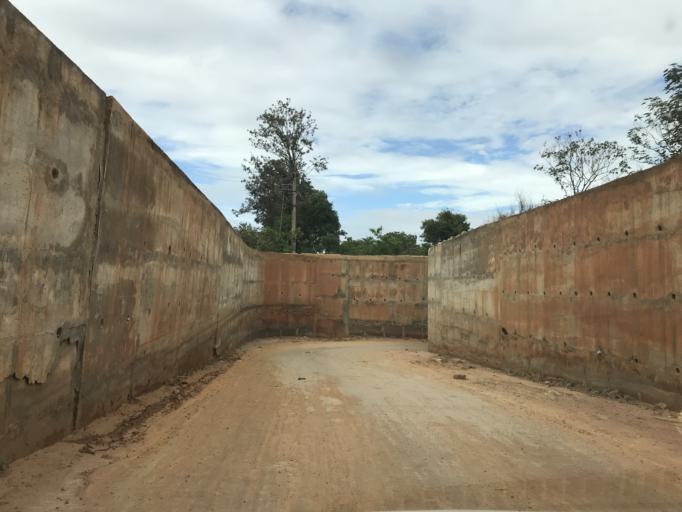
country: IN
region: Karnataka
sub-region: Bangalore Rural
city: Devanhalli
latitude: 13.2053
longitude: 77.6691
